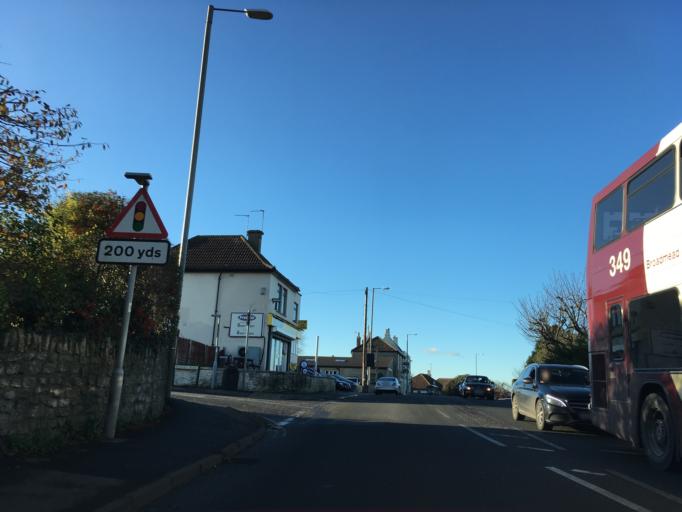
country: GB
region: England
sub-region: Bath and North East Somerset
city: Saltford
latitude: 51.4008
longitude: -2.4545
